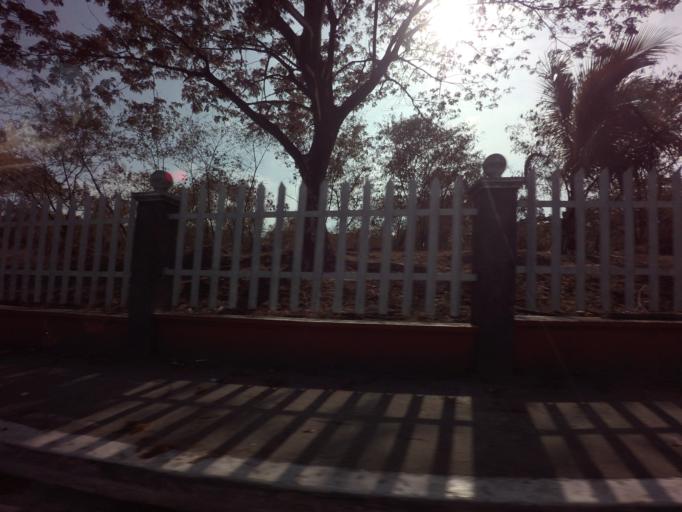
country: PH
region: Calabarzon
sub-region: Province of Rizal
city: Pateros
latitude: 14.5216
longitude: 121.0466
